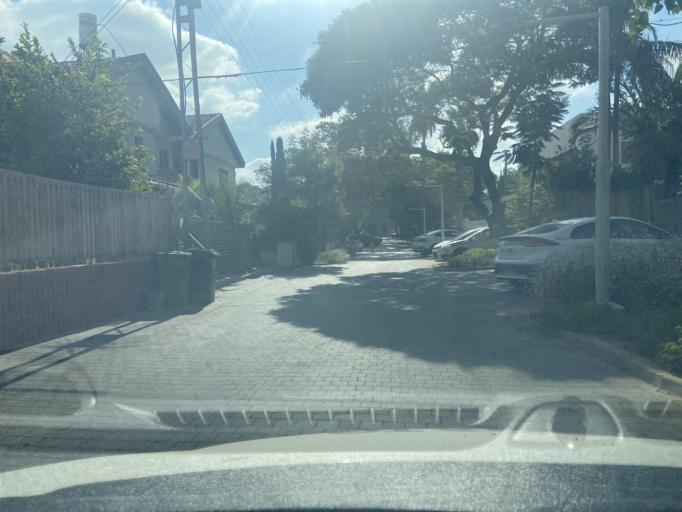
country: IL
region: Central District
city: Yehud
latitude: 32.0351
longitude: 34.8957
